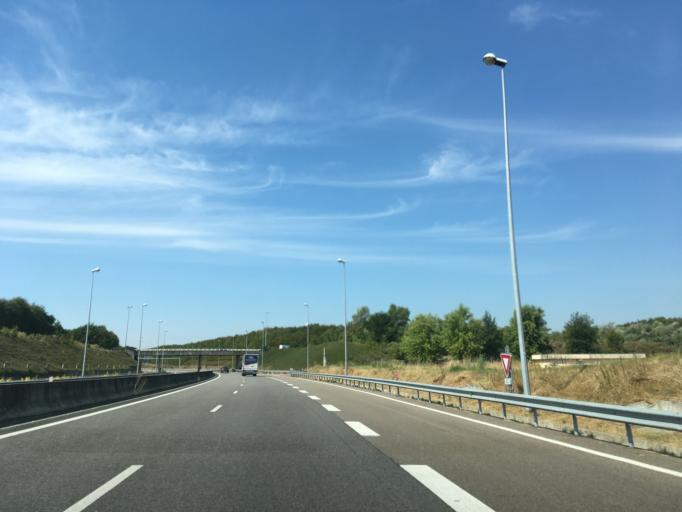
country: FR
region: Ile-de-France
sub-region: Departement des Yvelines
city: Chambourcy
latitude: 48.9139
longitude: 2.0426
